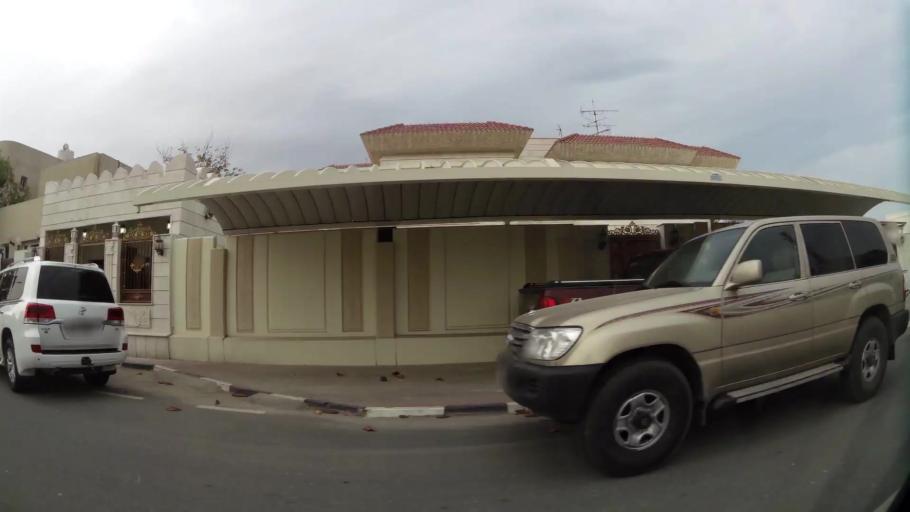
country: QA
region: Baladiyat ad Dawhah
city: Doha
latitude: 25.3289
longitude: 51.5072
